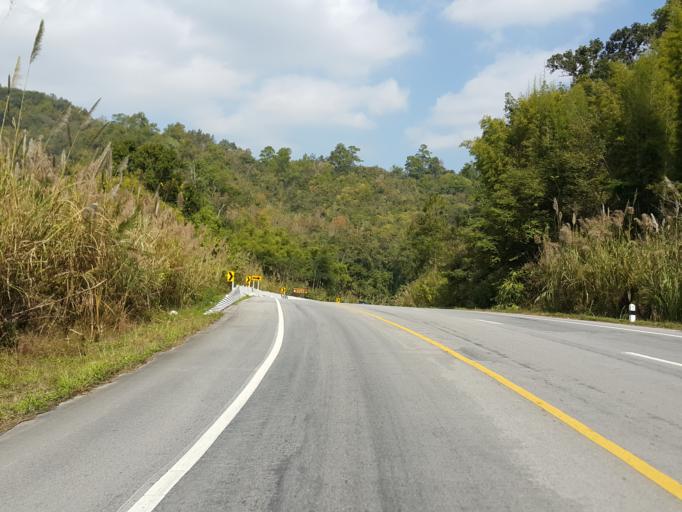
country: TH
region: Lampang
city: Wang Nuea
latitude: 19.0771
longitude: 99.3952
